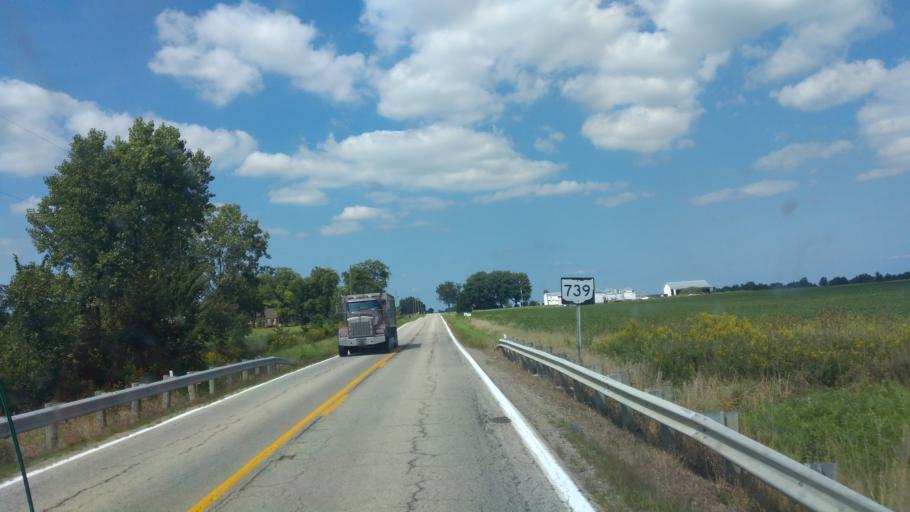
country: US
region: Ohio
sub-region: Union County
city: Marysville
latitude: 40.3646
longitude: -83.4545
